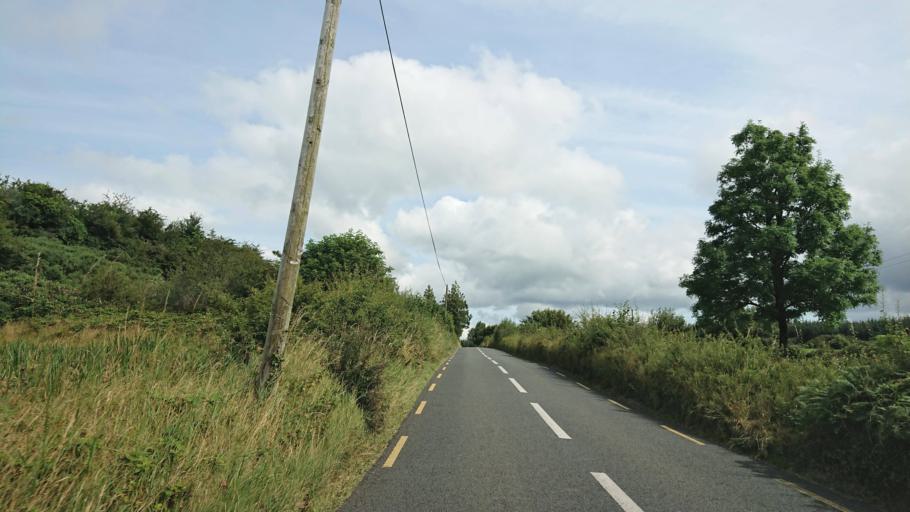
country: IE
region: Connaught
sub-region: County Leitrim
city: Carrick-on-Shannon
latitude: 54.0132
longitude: -8.1784
